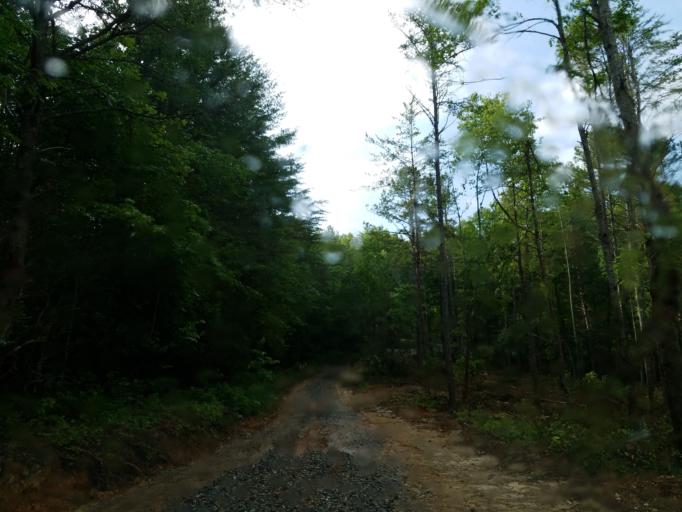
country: US
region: Georgia
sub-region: Fannin County
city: Blue Ridge
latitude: 34.7265
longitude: -84.2054
